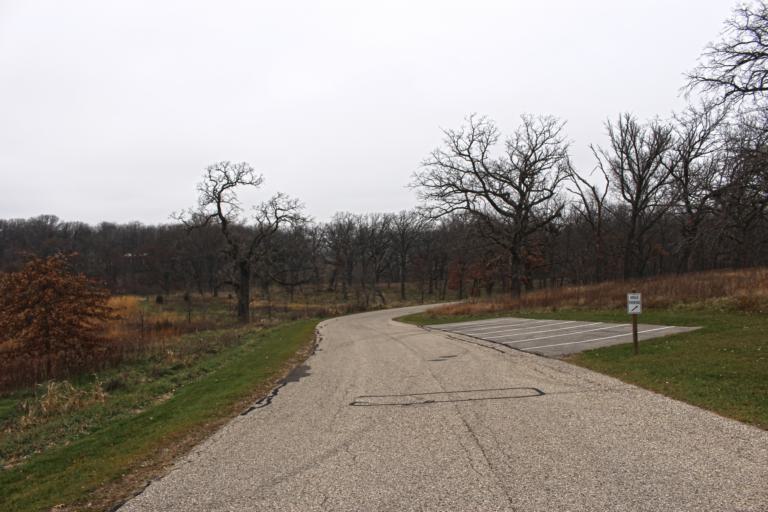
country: US
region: Wisconsin
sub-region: Jefferson County
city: Lake Mills
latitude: 43.0752
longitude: -88.9489
